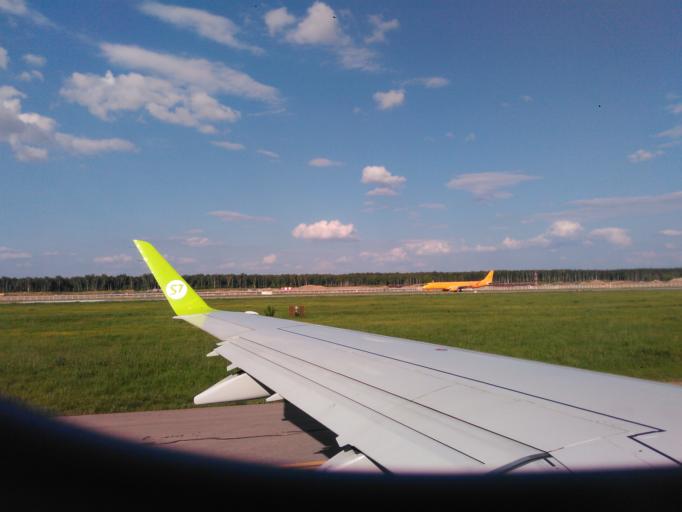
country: RU
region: Moskovskaya
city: Yakovlevskoye
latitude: 55.3978
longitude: 37.9335
